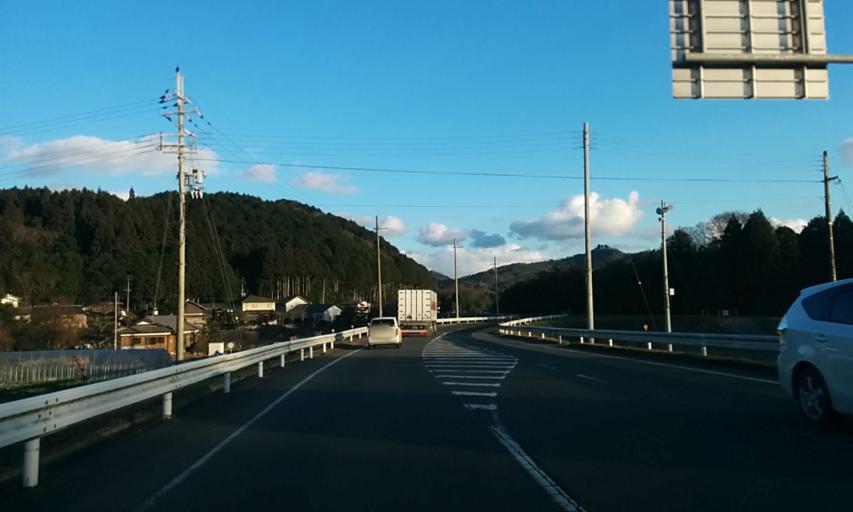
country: JP
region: Kyoto
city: Ayabe
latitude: 35.3114
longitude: 135.2598
